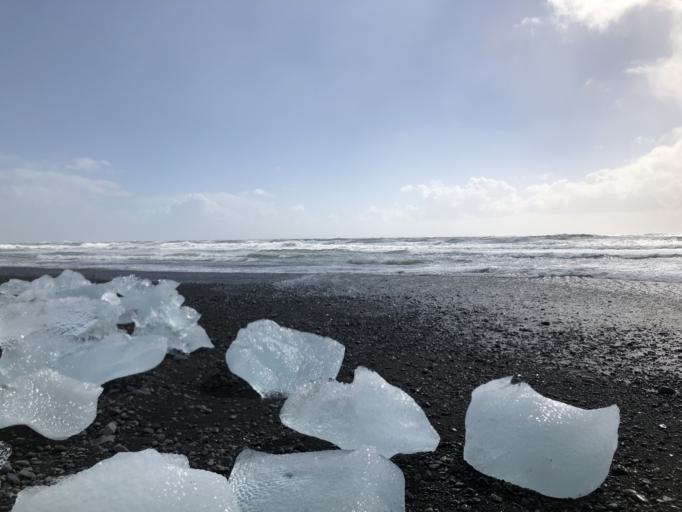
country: IS
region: East
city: Hoefn
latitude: 64.0430
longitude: -16.1767
